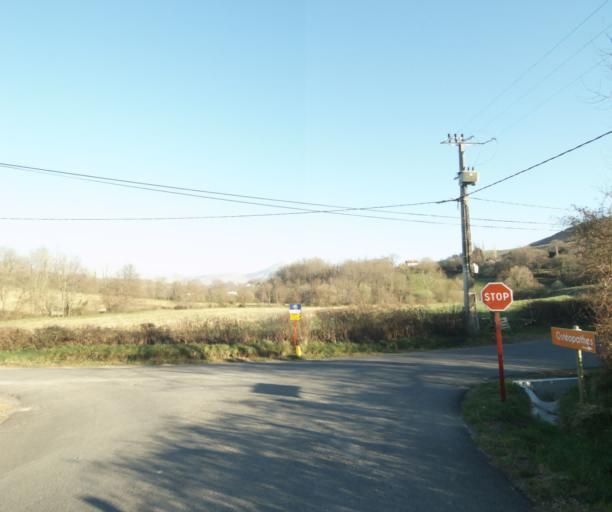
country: FR
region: Aquitaine
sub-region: Departement des Pyrenees-Atlantiques
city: Urrugne
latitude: 43.3476
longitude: -1.7167
